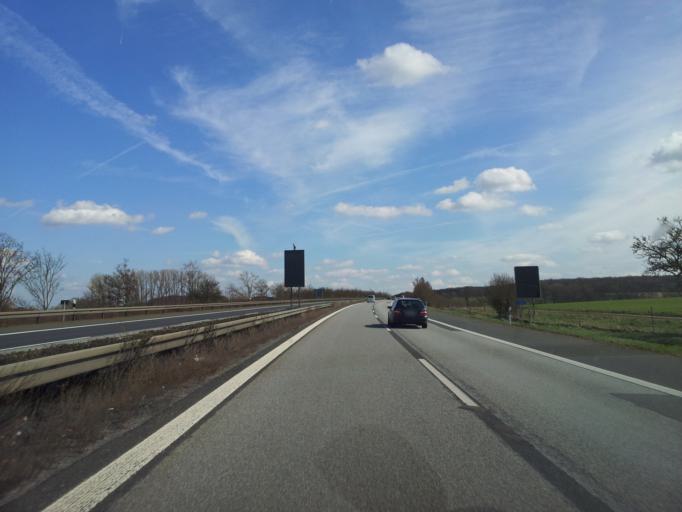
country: DE
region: Bavaria
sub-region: Regierungsbezirk Unterfranken
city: Gadheim
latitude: 50.0174
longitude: 10.3363
